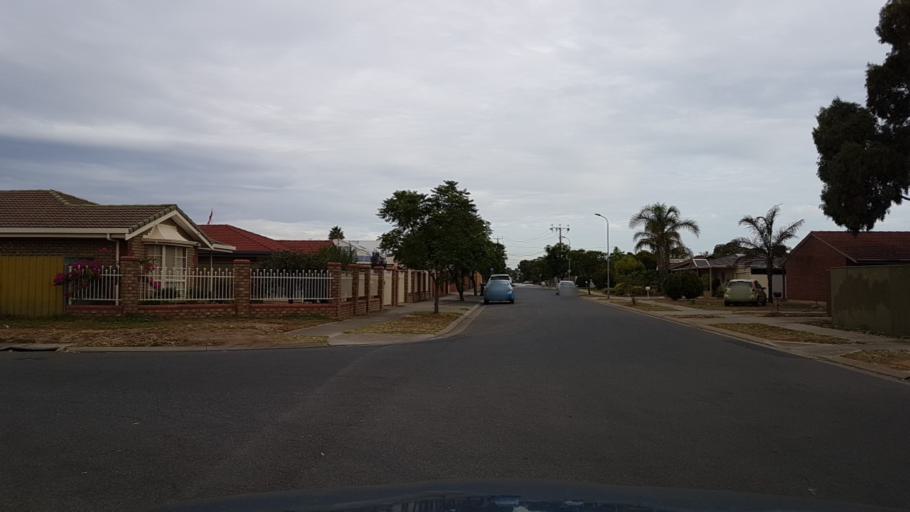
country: AU
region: South Australia
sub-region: Port Adelaide Enfield
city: Alberton
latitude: -34.8574
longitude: 138.5357
